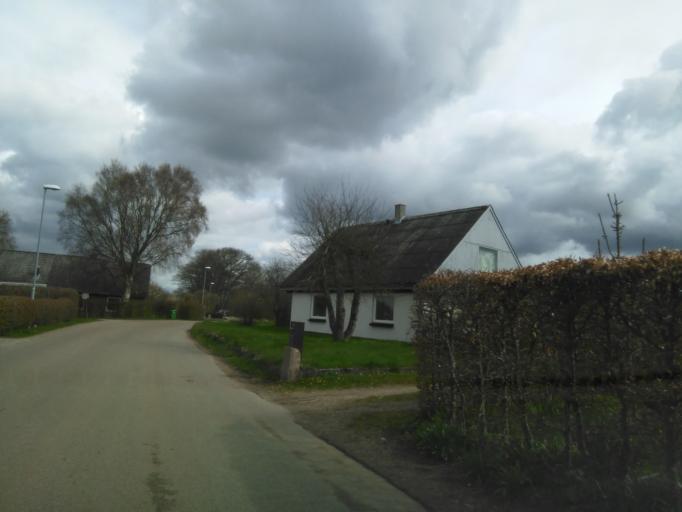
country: DK
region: Central Jutland
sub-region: Favrskov Kommune
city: Soften
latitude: 56.2165
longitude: 10.0821
